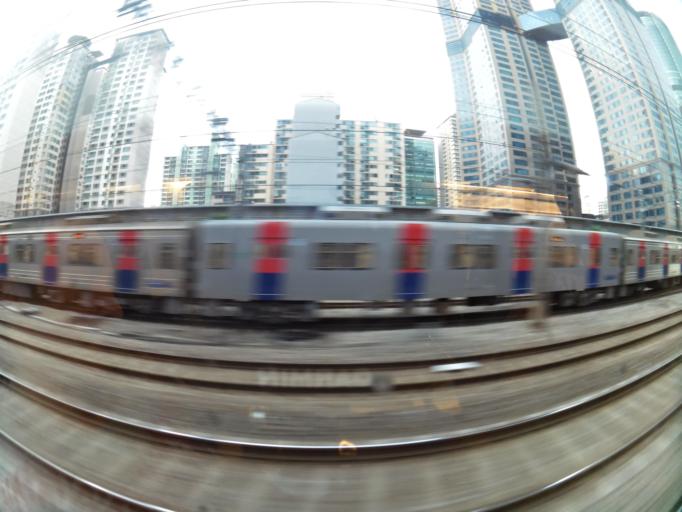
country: KR
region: Gyeonggi-do
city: Kwangmyong
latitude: 37.5069
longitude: 126.8879
